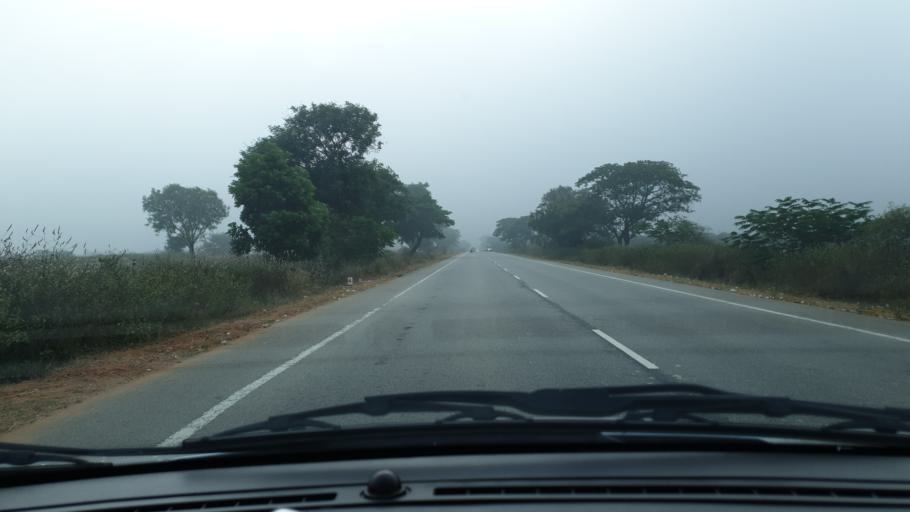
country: IN
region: Telangana
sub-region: Nalgonda
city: Devarkonda
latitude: 16.6386
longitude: 78.6332
